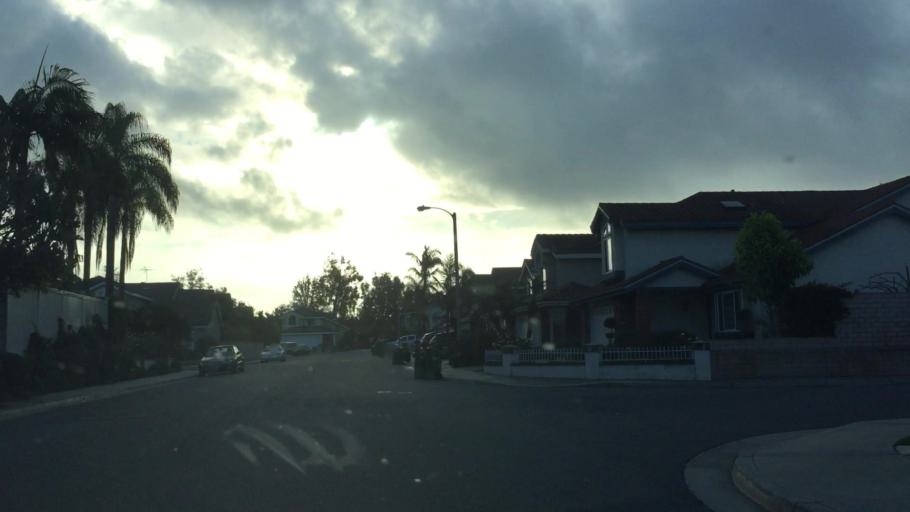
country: US
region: California
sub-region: Orange County
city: North Tustin
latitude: 33.7088
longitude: -117.7723
